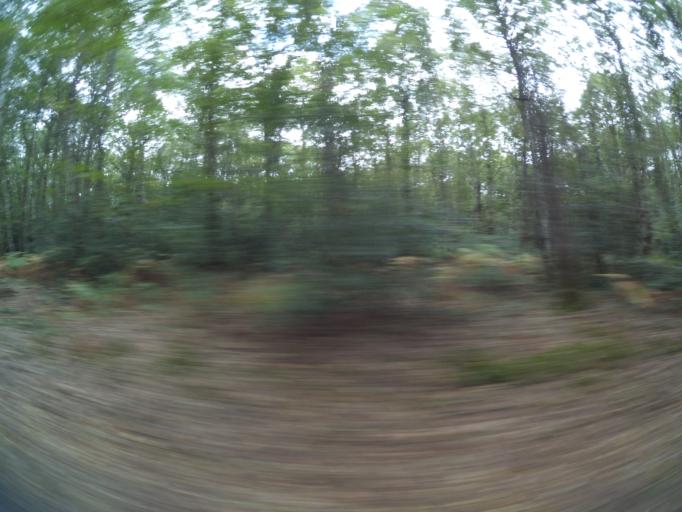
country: FR
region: Centre
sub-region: Departement d'Indre-et-Loire
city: Poce-sur-Cisse
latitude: 47.4814
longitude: 0.9843
